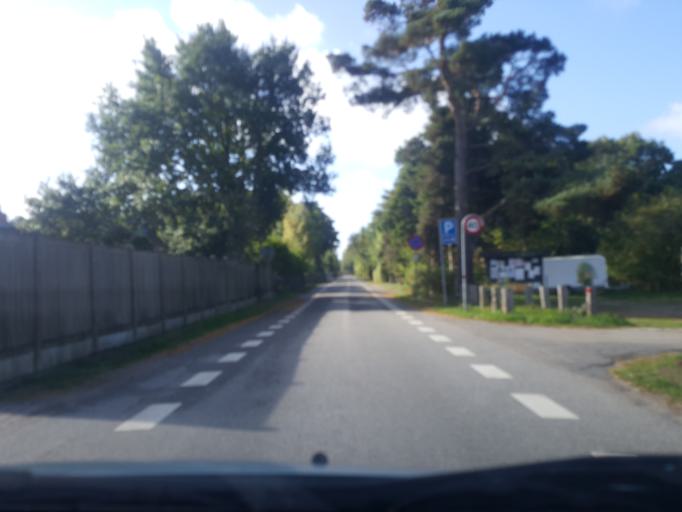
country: DK
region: Zealand
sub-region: Guldborgsund Kommune
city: Nykobing Falster
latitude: 54.6768
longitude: 11.9600
